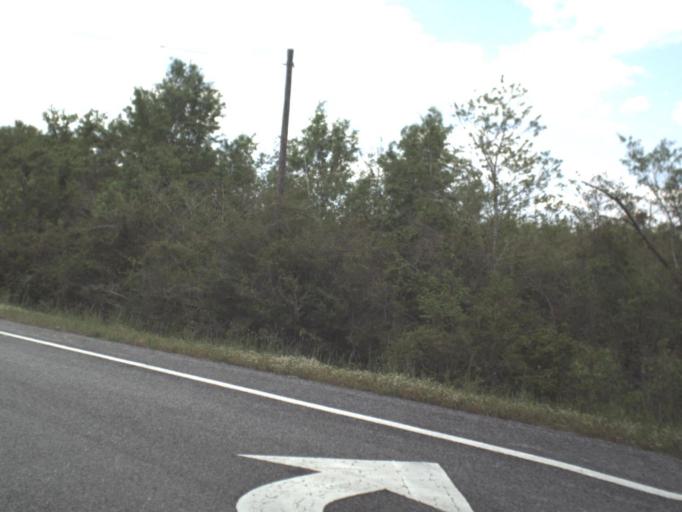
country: US
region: Florida
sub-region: Escambia County
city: Molino
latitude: 30.7950
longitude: -87.3338
